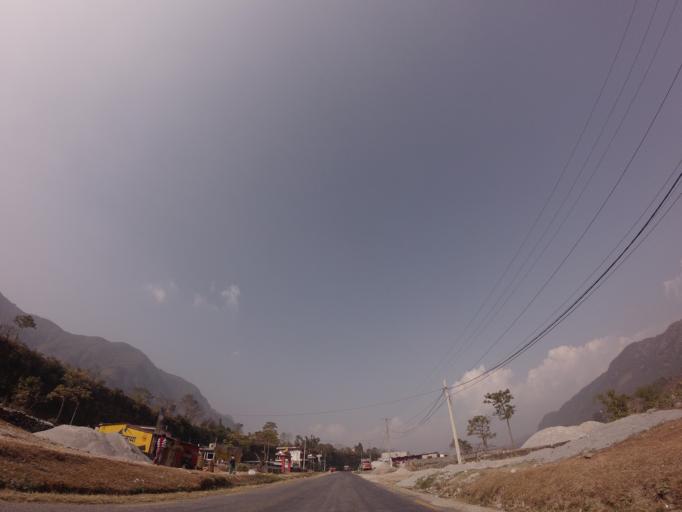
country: NP
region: Western Region
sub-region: Gandaki Zone
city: Pokhara
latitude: 28.2586
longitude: 83.9614
